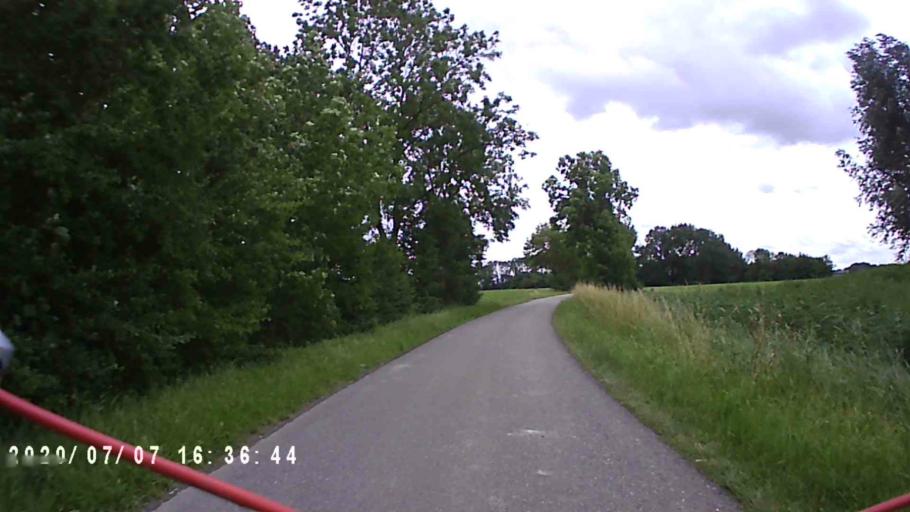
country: NL
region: Groningen
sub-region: Gemeente Winsum
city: Winsum
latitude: 53.3545
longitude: 6.5349
